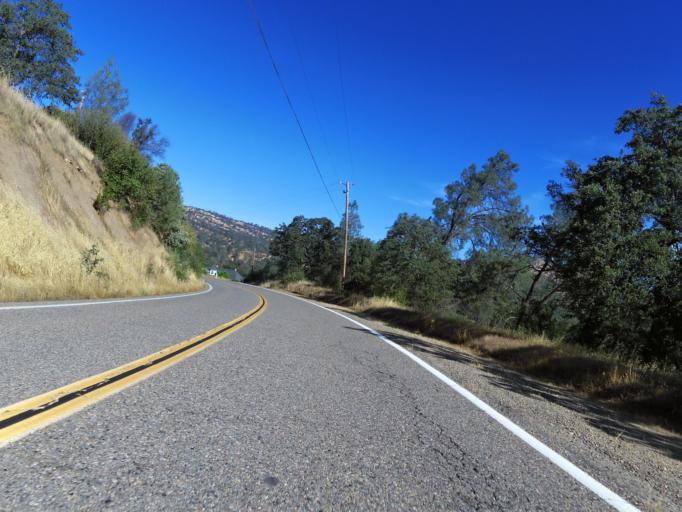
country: US
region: California
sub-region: Madera County
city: Yosemite Lakes
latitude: 37.2102
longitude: -119.7903
